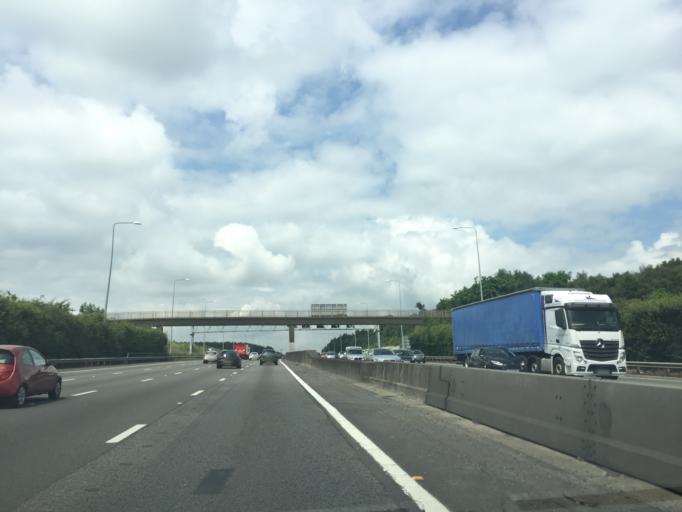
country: GB
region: England
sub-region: Buckinghamshire
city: Gerrards Cross
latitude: 51.5877
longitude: -0.5337
